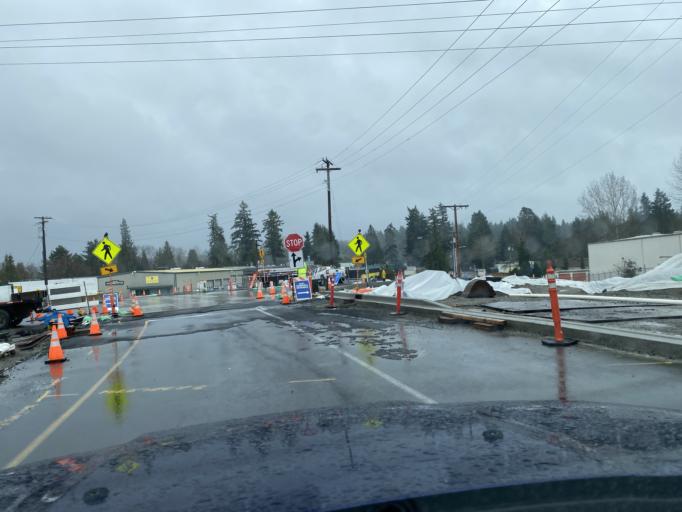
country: US
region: Washington
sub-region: King County
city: Bellevue
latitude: 47.6244
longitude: -122.1596
